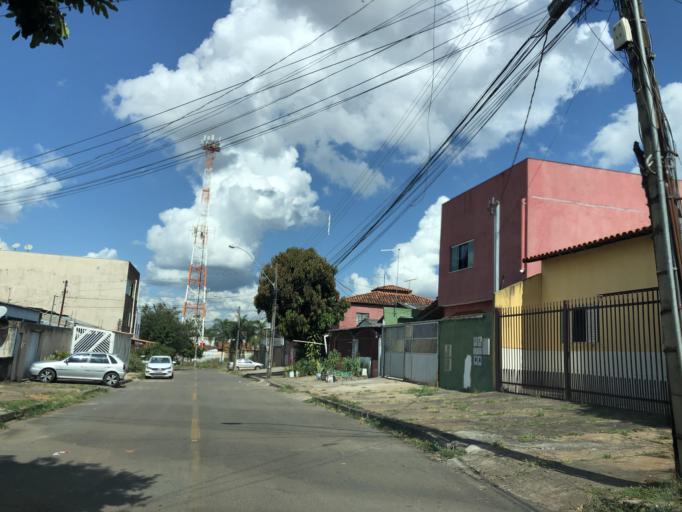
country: BR
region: Federal District
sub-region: Brasilia
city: Brasilia
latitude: -15.8996
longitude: -47.7782
